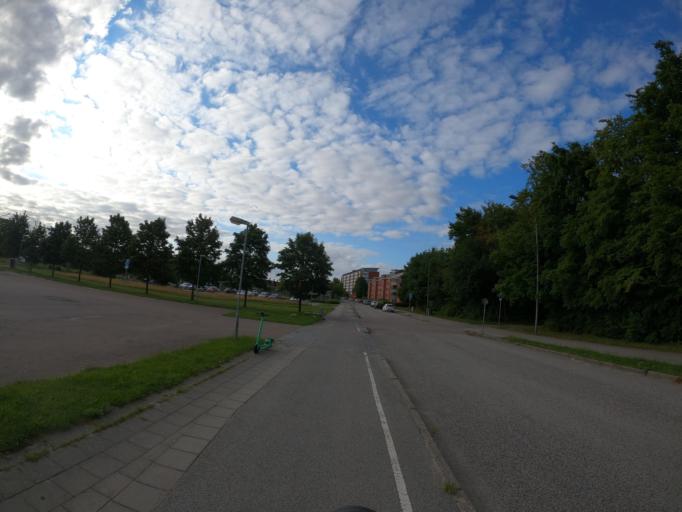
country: SE
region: Skane
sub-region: Lunds Kommun
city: Lund
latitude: 55.6939
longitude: 13.1831
